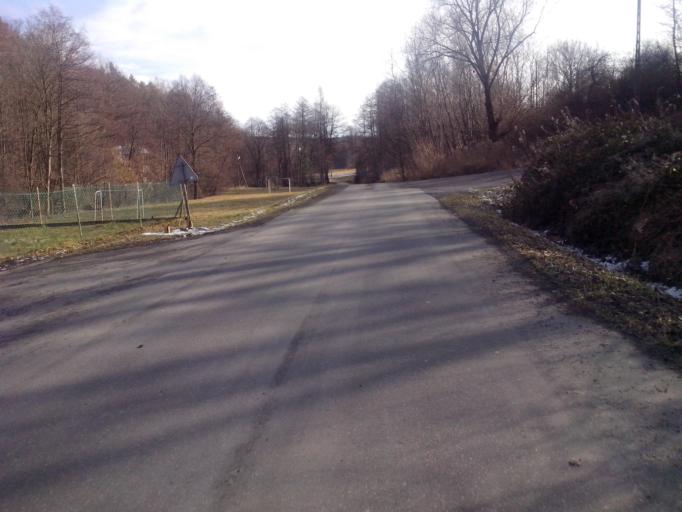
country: PL
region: Subcarpathian Voivodeship
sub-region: Powiat strzyzowski
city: Strzyzow
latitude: 49.7996
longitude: 21.8069
